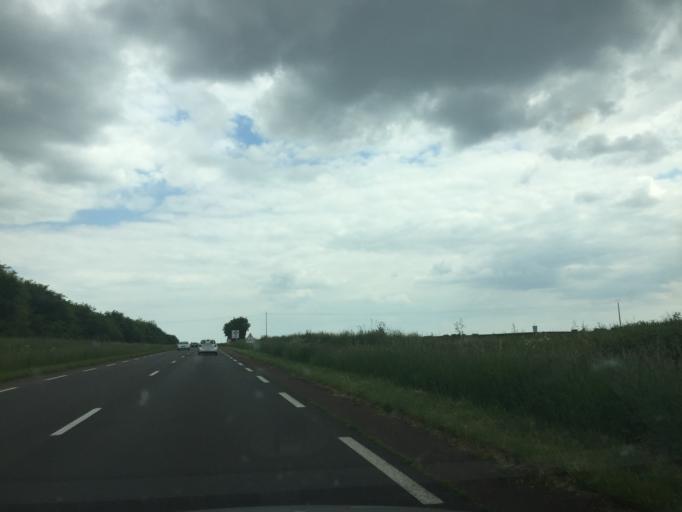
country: FR
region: Pays de la Loire
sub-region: Departement de la Vendee
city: Benet
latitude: 46.3833
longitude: -0.6142
